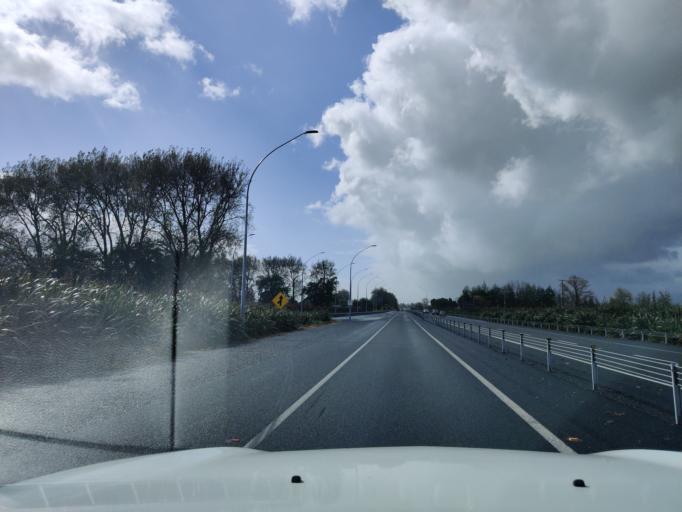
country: NZ
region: Waikato
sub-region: Waipa District
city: Cambridge
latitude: -37.8965
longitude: 175.5075
